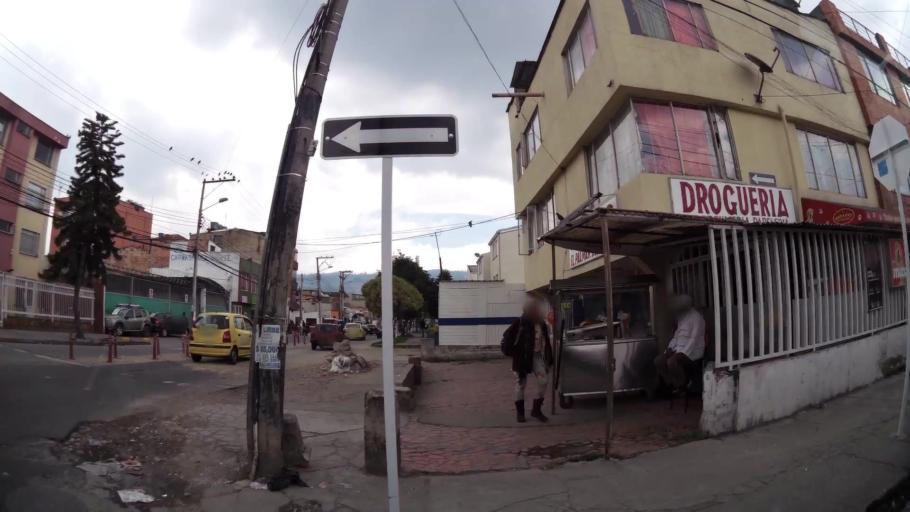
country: CO
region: Cundinamarca
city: La Calera
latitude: 4.7441
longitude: -74.0427
